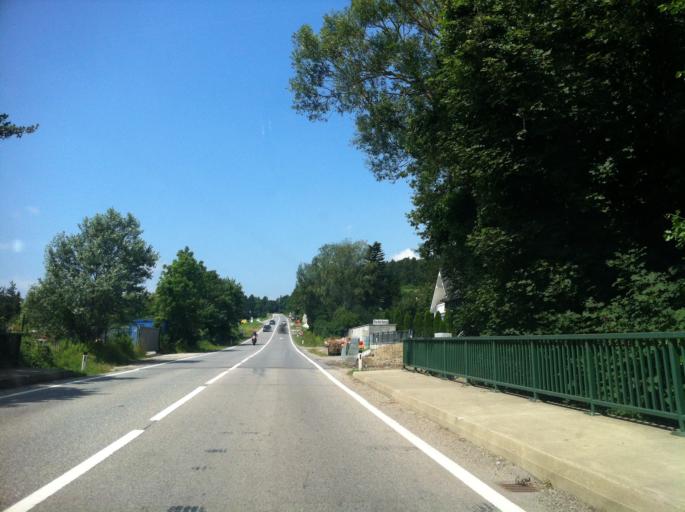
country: AT
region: Lower Austria
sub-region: Politischer Bezirk Wien-Umgebung
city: Gablitz
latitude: 48.2425
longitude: 16.1214
